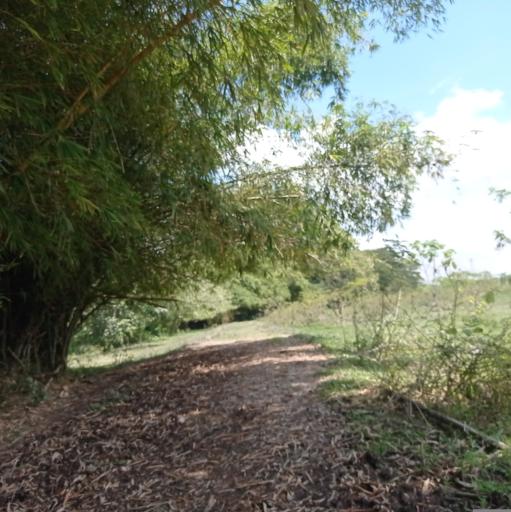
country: CO
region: Santander
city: Barrancabermeja
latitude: 7.1039
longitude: -73.8787
